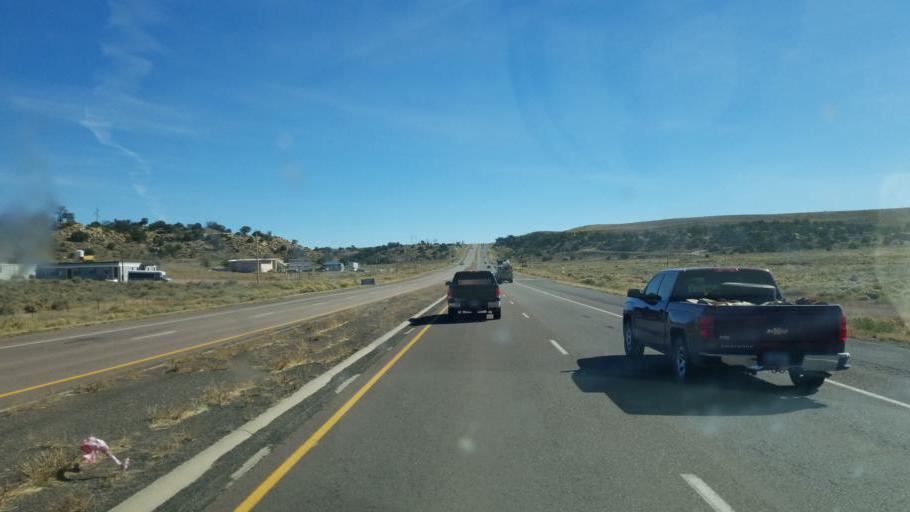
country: US
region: Arizona
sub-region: Apache County
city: Window Rock
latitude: 35.6389
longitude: -109.0054
